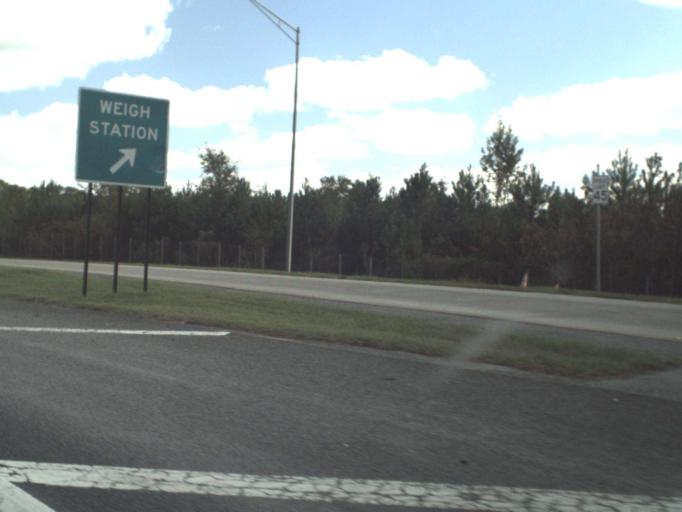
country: US
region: Florida
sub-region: Jackson County
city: Sneads
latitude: 30.6389
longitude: -84.9942
